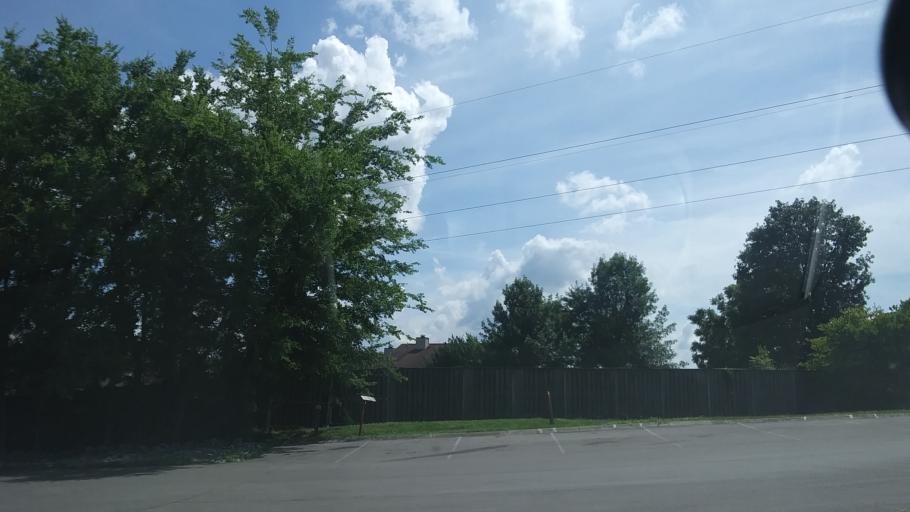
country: US
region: Tennessee
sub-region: Rutherford County
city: La Vergne
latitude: 36.0774
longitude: -86.6335
